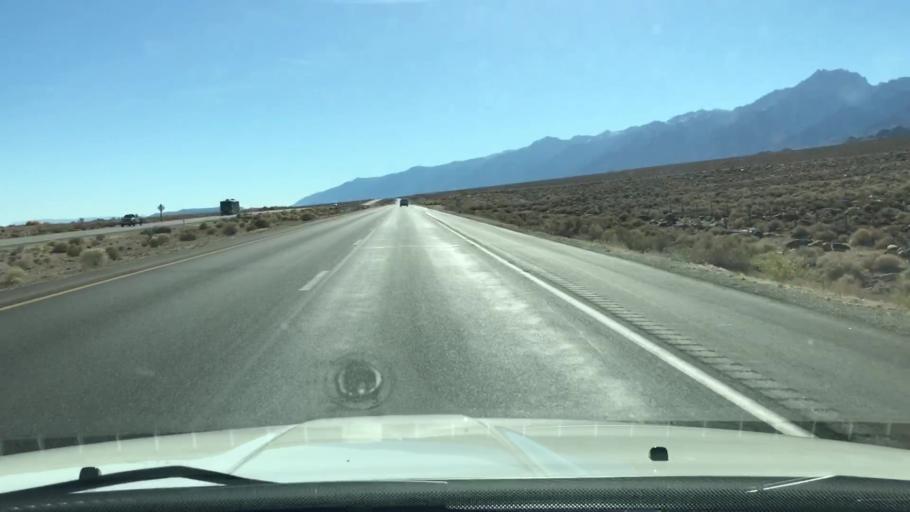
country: US
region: California
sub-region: Inyo County
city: Big Pine
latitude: 36.8693
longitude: -118.2370
